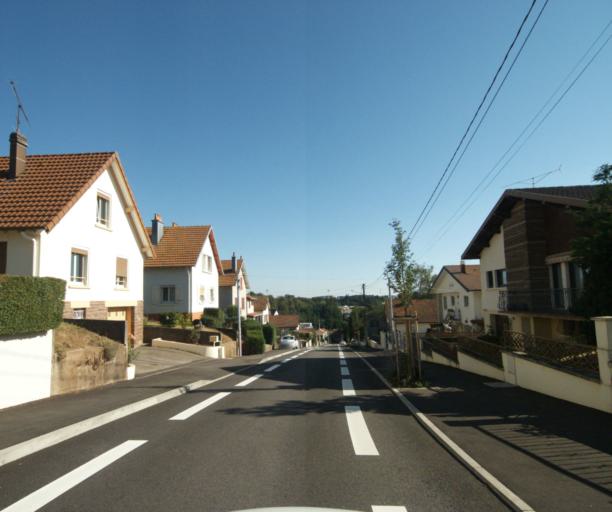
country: FR
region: Lorraine
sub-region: Departement des Vosges
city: Epinal
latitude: 48.1729
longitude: 6.4615
